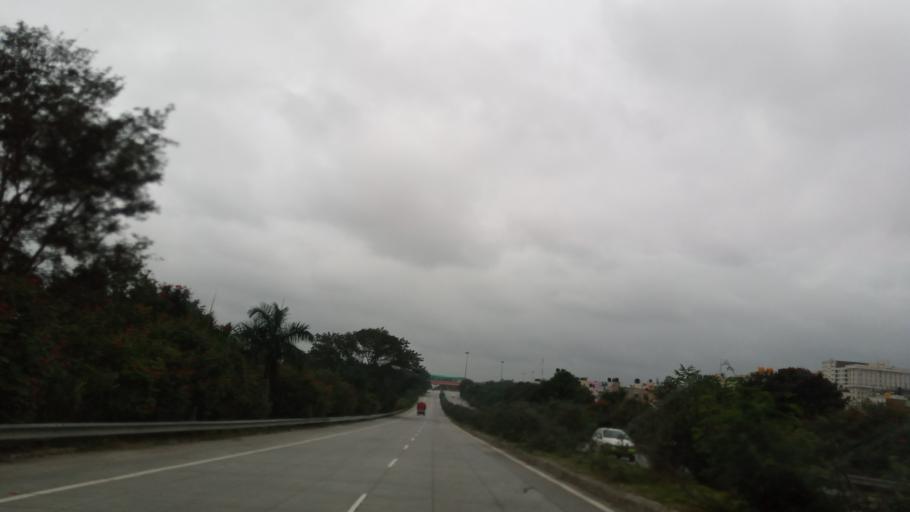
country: IN
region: Karnataka
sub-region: Bangalore Urban
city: Bangalore
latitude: 12.9304
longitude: 77.5316
